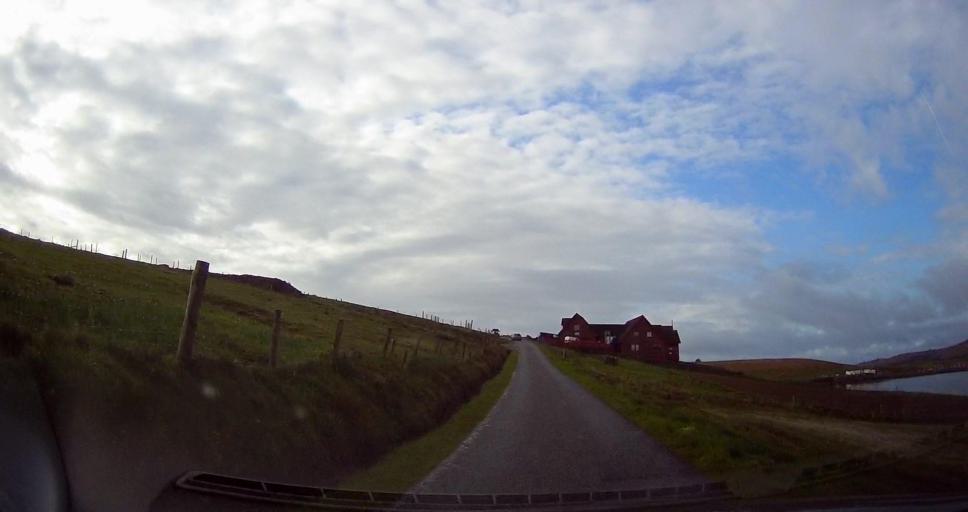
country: GB
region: Scotland
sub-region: Shetland Islands
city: Sandwick
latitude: 60.0455
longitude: -1.2067
